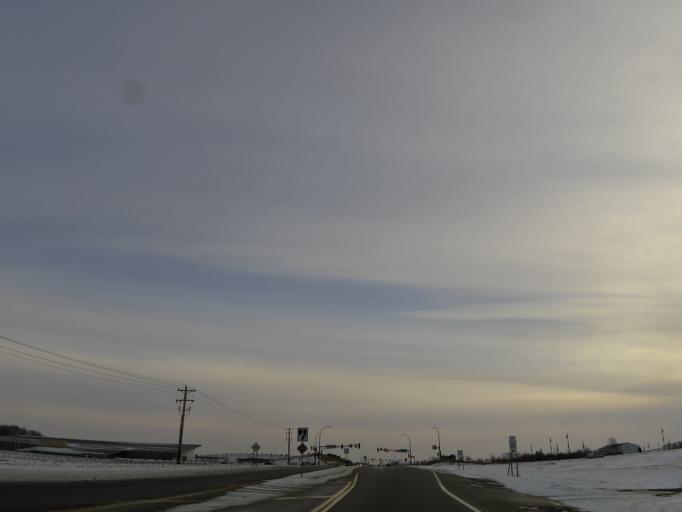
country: US
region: Minnesota
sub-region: Carver County
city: Carver
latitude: 44.7826
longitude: -93.6425
